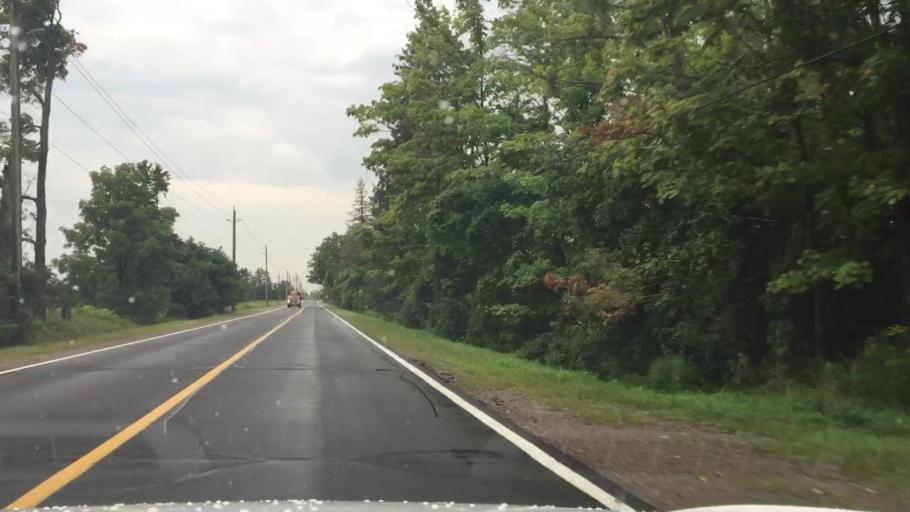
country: CA
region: Ontario
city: Markham
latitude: 43.8888
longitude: -79.2116
